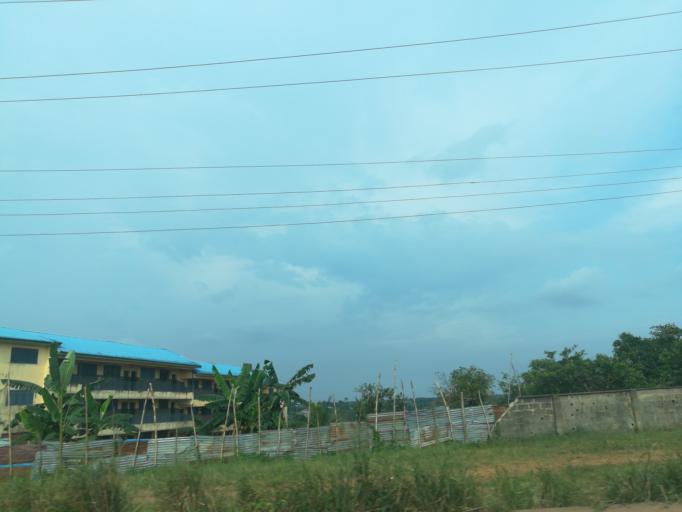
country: NG
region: Lagos
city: Ikorodu
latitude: 6.6560
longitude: 3.6691
